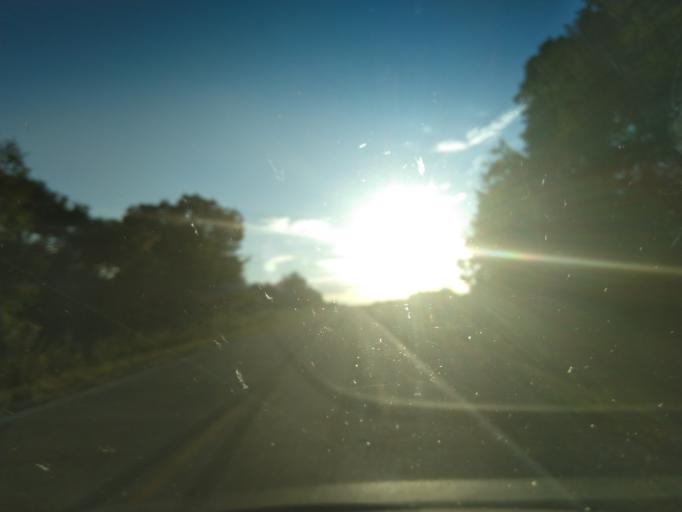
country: US
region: Iowa
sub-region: Jackson County
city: Maquoketa
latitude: 42.1644
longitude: -90.6896
